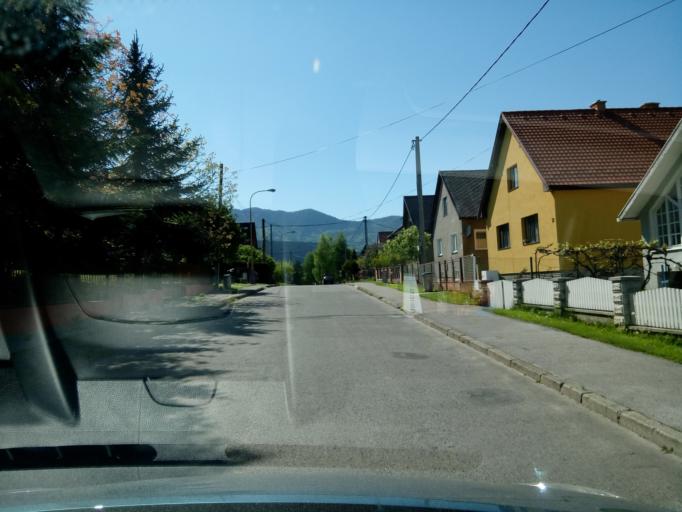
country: SK
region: Zilinsky
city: Ruzomberok
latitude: 49.0802
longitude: 19.2935
